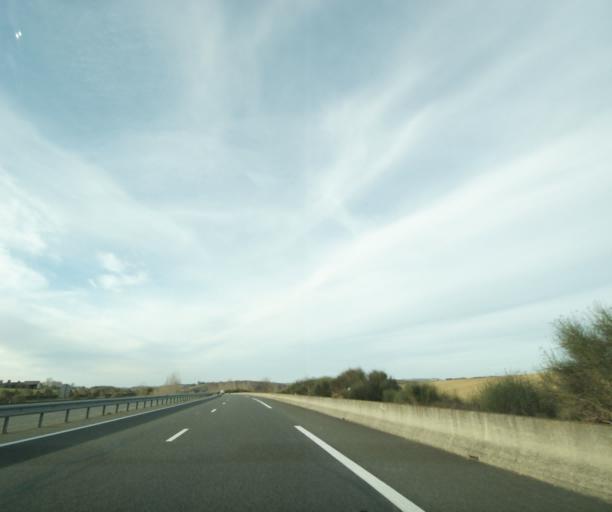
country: FR
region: Midi-Pyrenees
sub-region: Departement du Gers
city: Aubiet
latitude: 43.6513
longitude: 0.7917
